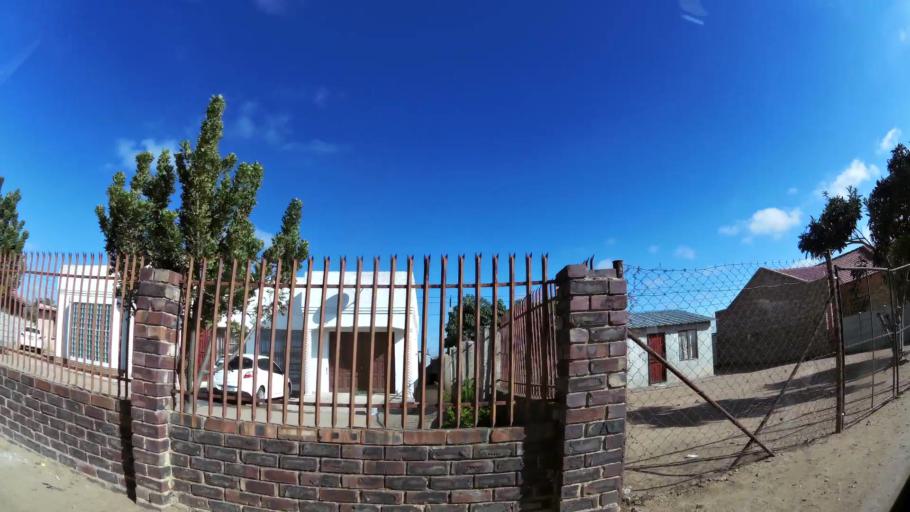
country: ZA
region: Limpopo
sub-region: Capricorn District Municipality
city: Polokwane
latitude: -23.8472
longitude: 29.4018
